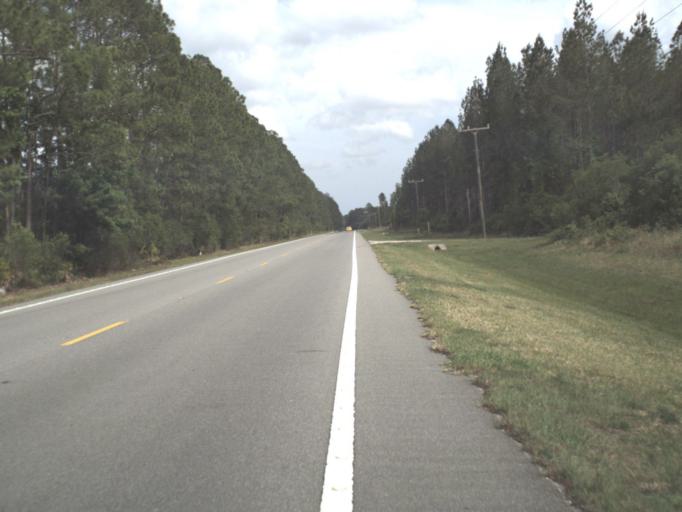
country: US
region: Florida
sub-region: Flagler County
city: Bunnell
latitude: 29.4739
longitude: -81.3276
